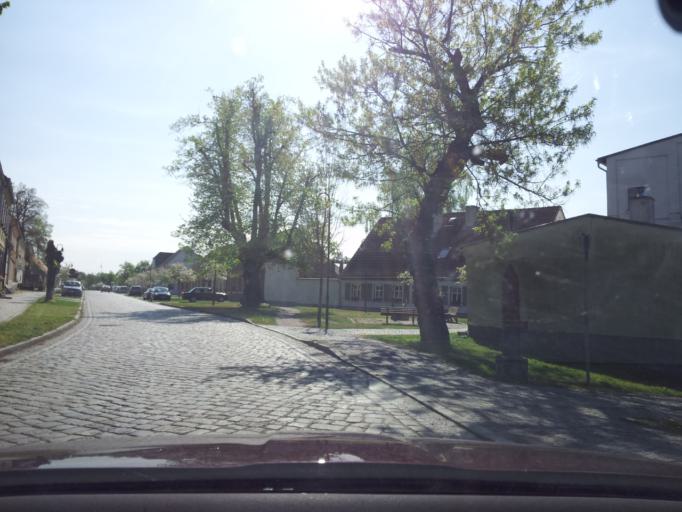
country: DE
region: Brandenburg
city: Juterbog
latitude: 52.0249
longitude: 13.1008
